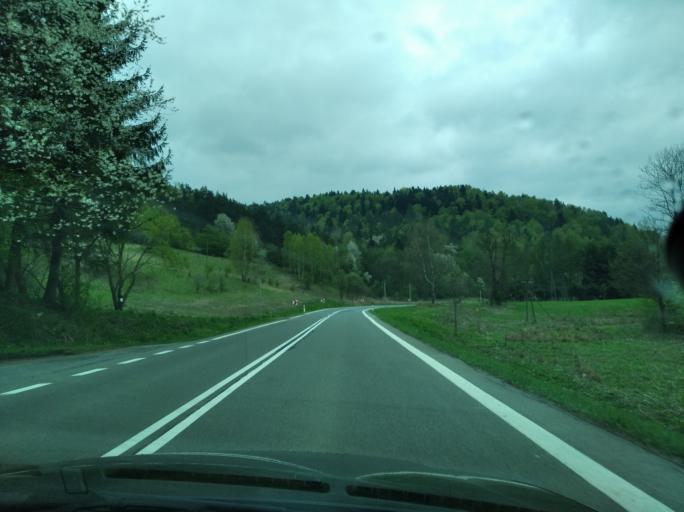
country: PL
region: Subcarpathian Voivodeship
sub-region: Powiat sanocki
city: Zagorz
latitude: 49.5398
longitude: 22.3032
